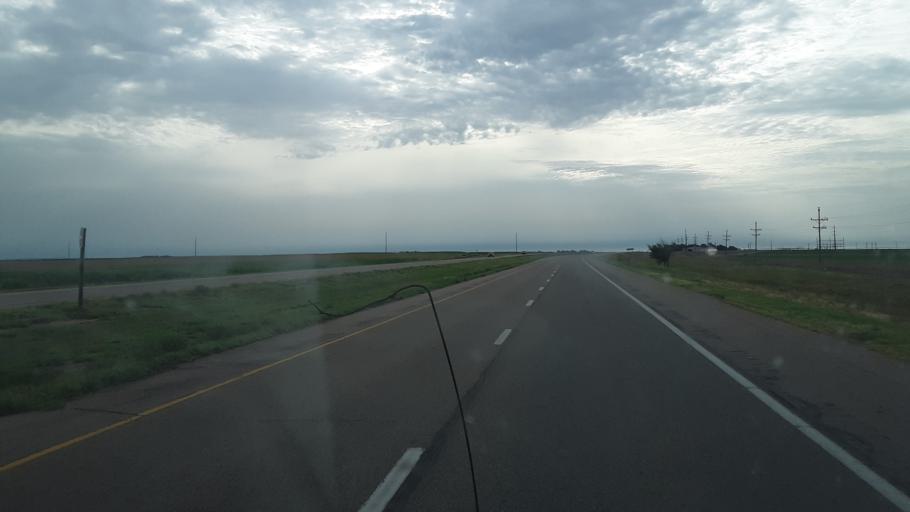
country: US
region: Kansas
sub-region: Finney County
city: Garden City
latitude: 37.9603
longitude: -100.7836
